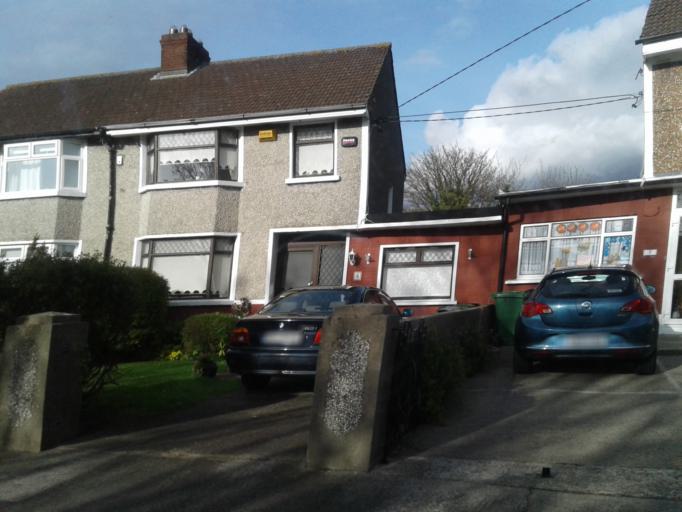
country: IE
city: Coolock
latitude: 53.3816
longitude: -6.2042
